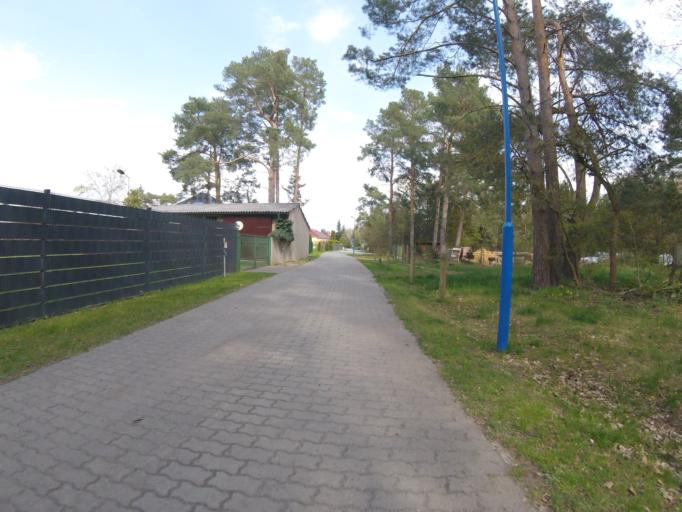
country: DE
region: Brandenburg
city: Bestensee
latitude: 52.2415
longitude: 13.6193
